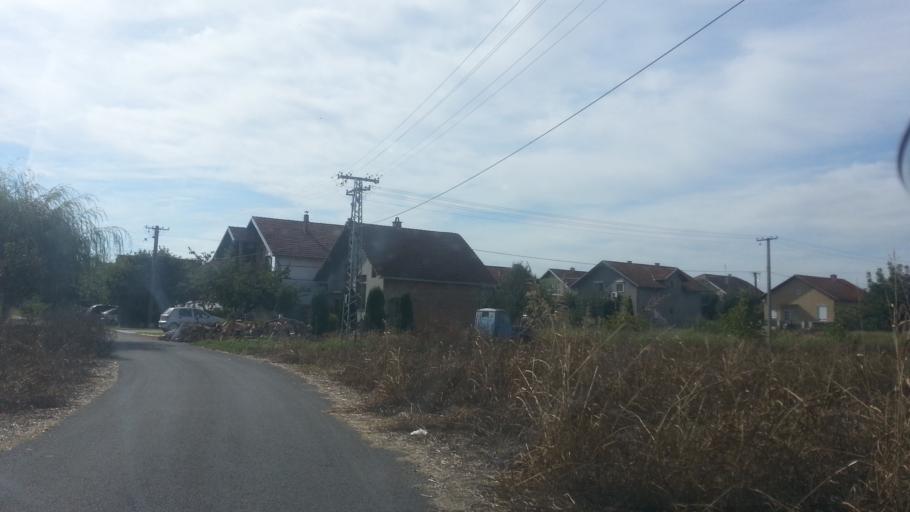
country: RS
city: Novi Banovci
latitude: 44.9689
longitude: 20.2751
